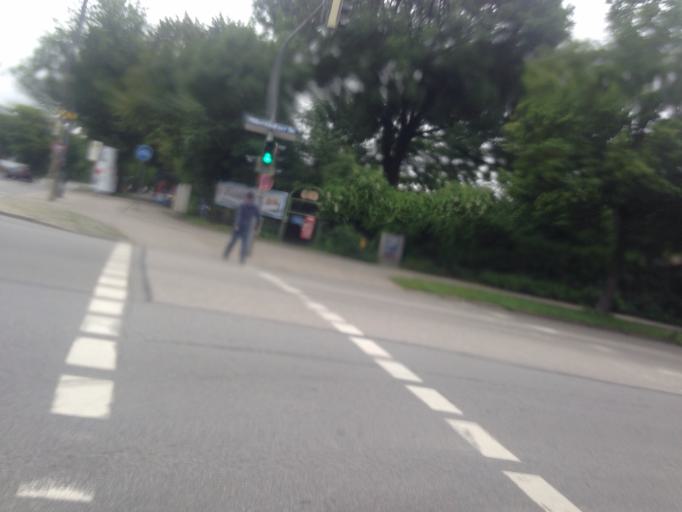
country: DE
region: Bavaria
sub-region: Upper Bavaria
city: Bogenhausen
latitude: 48.1844
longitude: 11.5845
